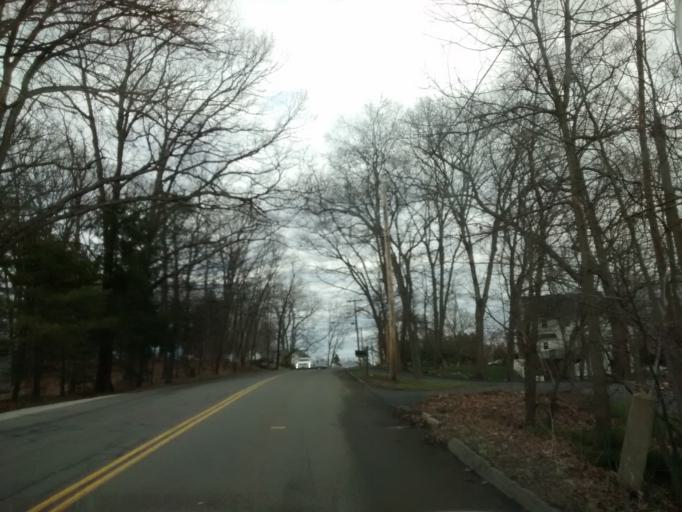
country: US
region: Massachusetts
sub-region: Worcester County
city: Grafton
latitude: 42.2414
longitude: -71.7181
